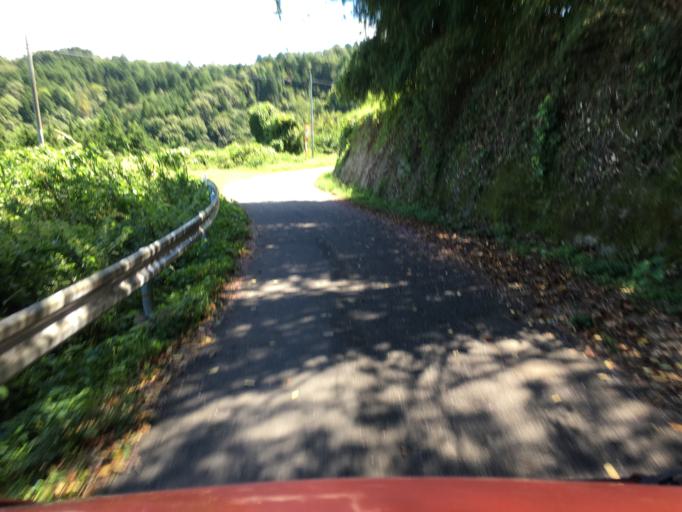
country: JP
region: Okayama
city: Tsuyama
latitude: 34.8992
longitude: 134.1352
